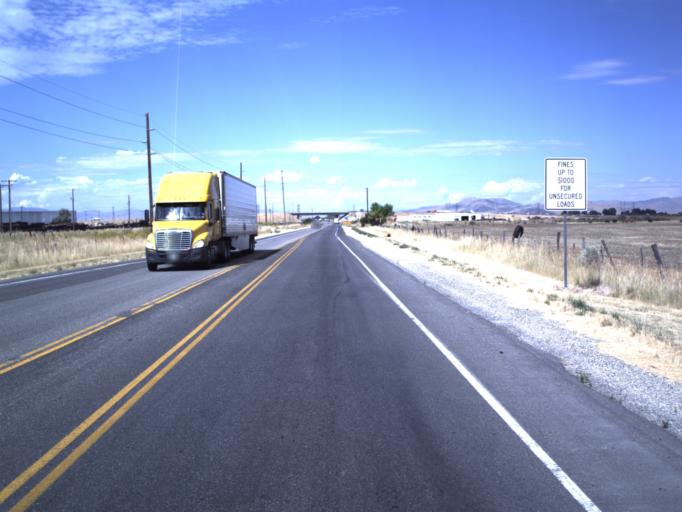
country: US
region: Utah
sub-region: Box Elder County
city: Brigham City
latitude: 41.5331
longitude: -112.0538
